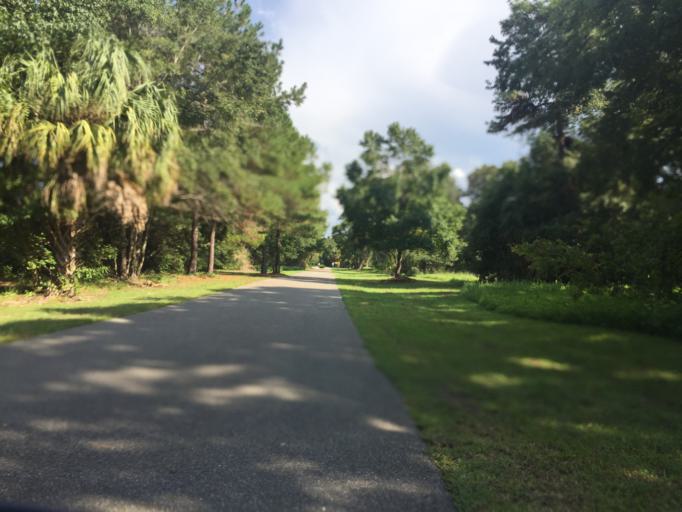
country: US
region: Florida
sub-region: Seminole County
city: Winter Springs
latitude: 28.6892
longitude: -81.2581
